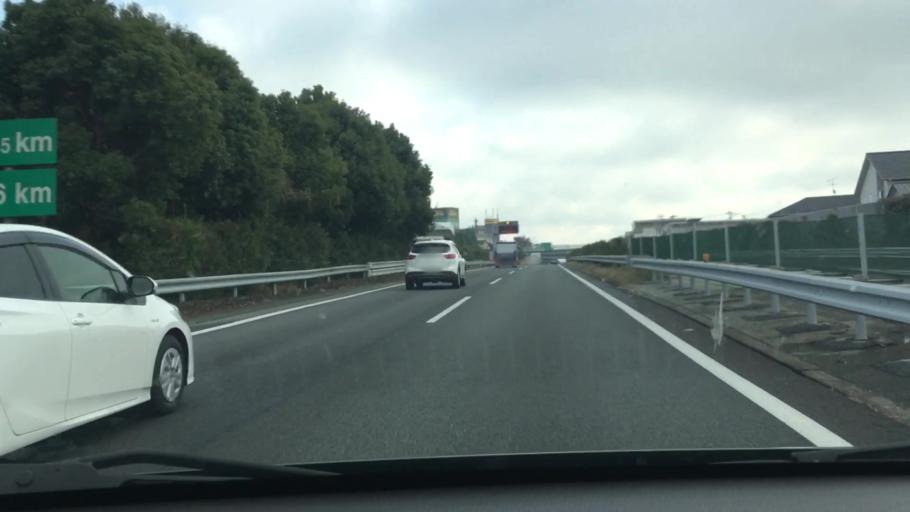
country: JP
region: Kumamoto
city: Kumamoto
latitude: 32.8401
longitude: 130.7754
